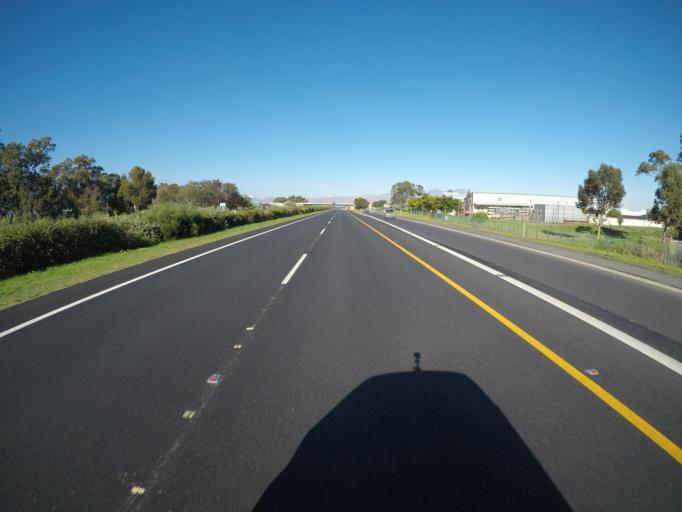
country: ZA
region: Western Cape
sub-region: Cape Winelands District Municipality
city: Stellenbosch
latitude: -34.0747
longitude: 18.8181
